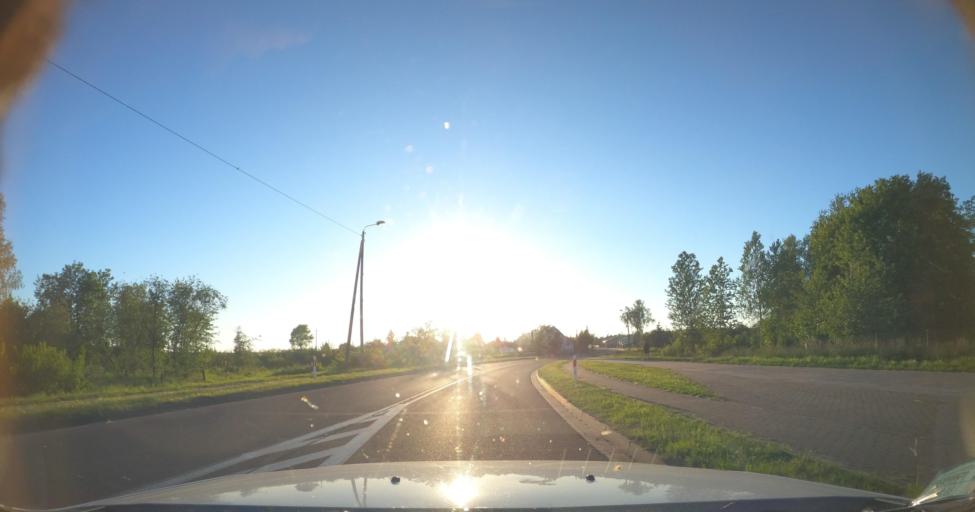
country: PL
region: Pomeranian Voivodeship
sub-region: Powiat slupski
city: Potegowo
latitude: 54.4208
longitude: 17.3827
